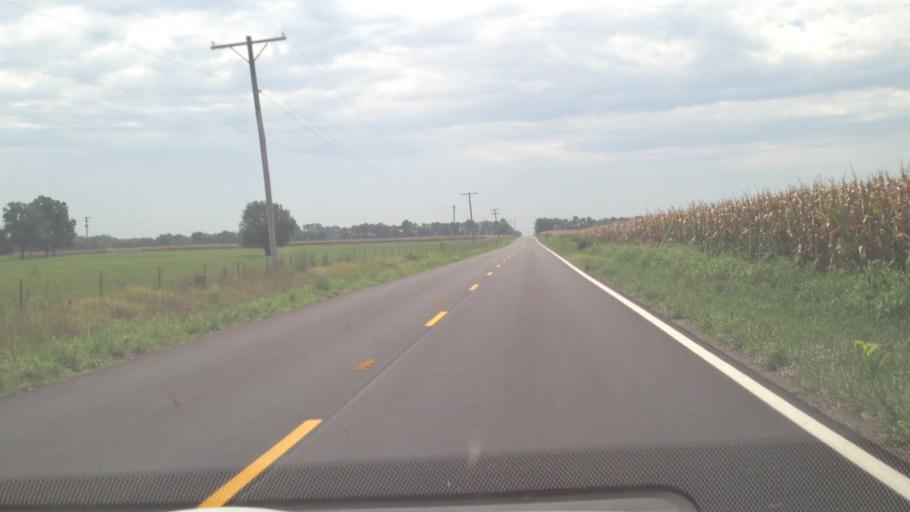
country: US
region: Kansas
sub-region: Crawford County
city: Girard
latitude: 37.6446
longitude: -94.9698
